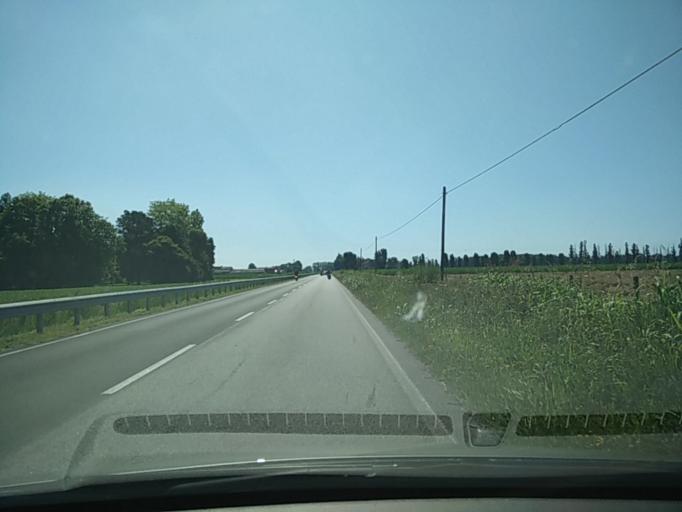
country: IT
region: Veneto
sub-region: Provincia di Venezia
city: San Giorgio di Livenza
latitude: 45.6231
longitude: 12.7939
